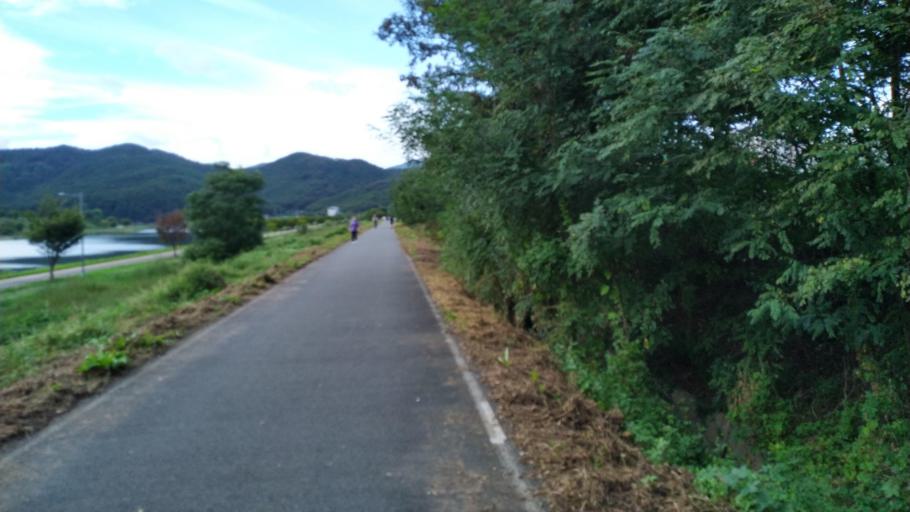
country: KR
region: Daegu
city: Daegu
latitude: 35.9193
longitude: 128.6334
